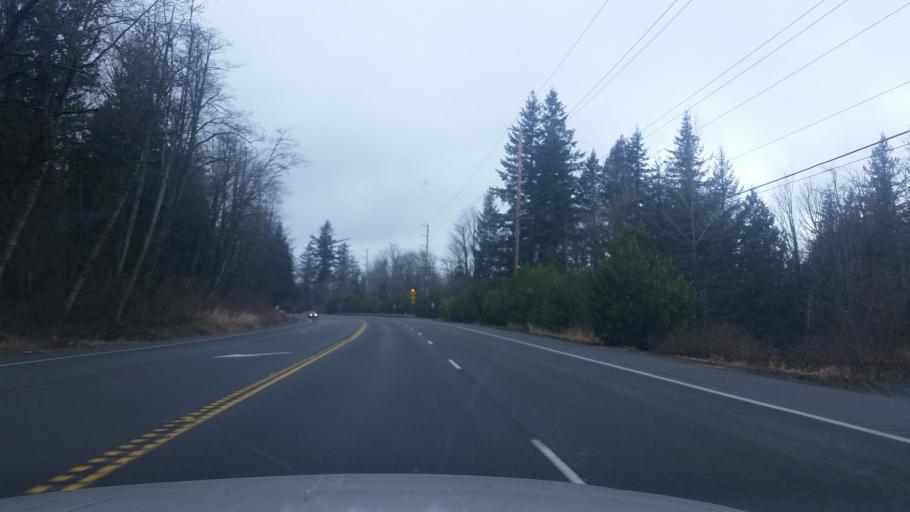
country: US
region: Washington
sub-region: King County
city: Snoqualmie
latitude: 47.5158
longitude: -121.8350
